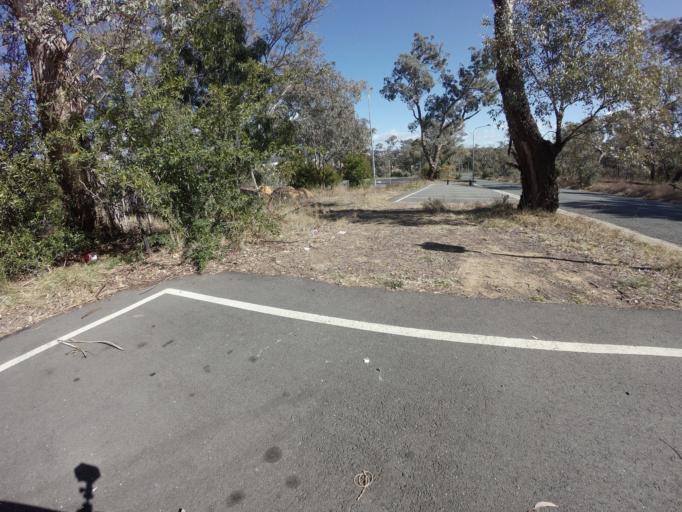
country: AU
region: Australian Capital Territory
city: Canberra
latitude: -35.2935
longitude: 149.1490
